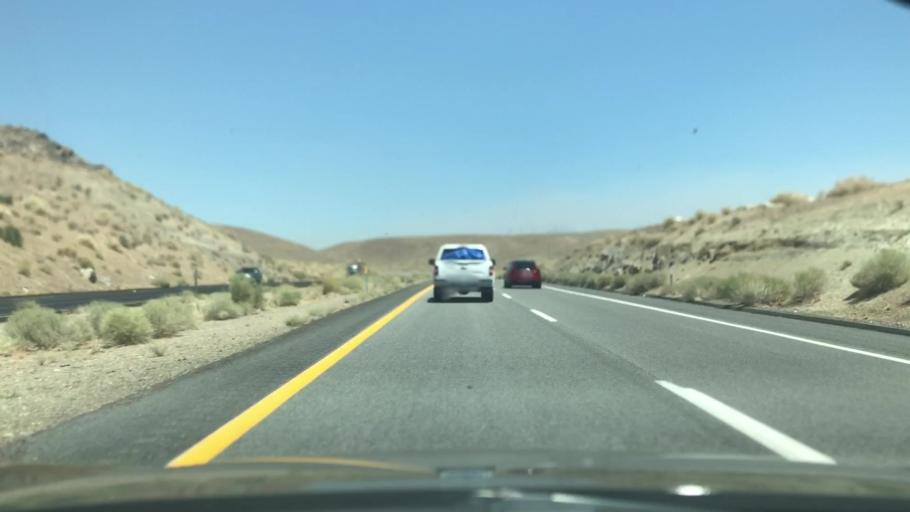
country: US
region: California
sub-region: Inyo County
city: Big Pine
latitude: 37.0485
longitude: -118.2333
